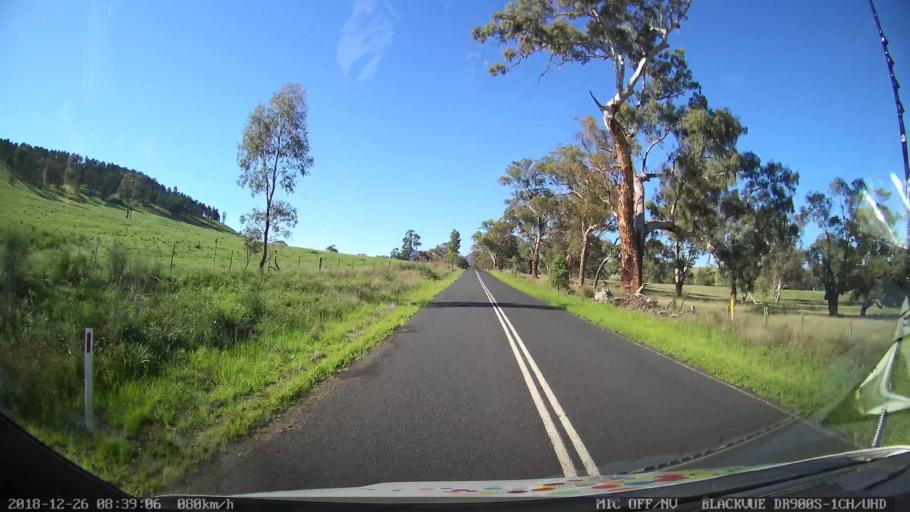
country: AU
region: New South Wales
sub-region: Upper Hunter Shire
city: Merriwa
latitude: -32.4494
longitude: 150.0767
